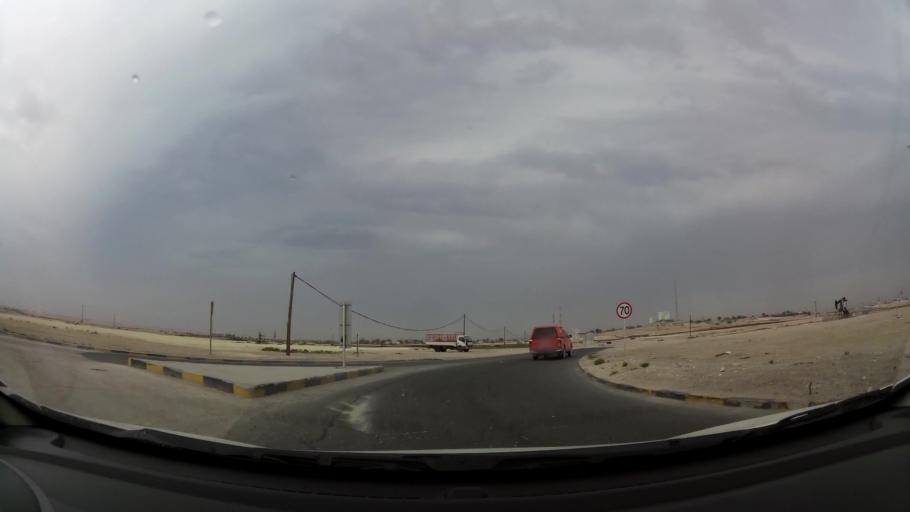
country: BH
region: Central Governorate
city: Dar Kulayb
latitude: 26.0742
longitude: 50.5517
